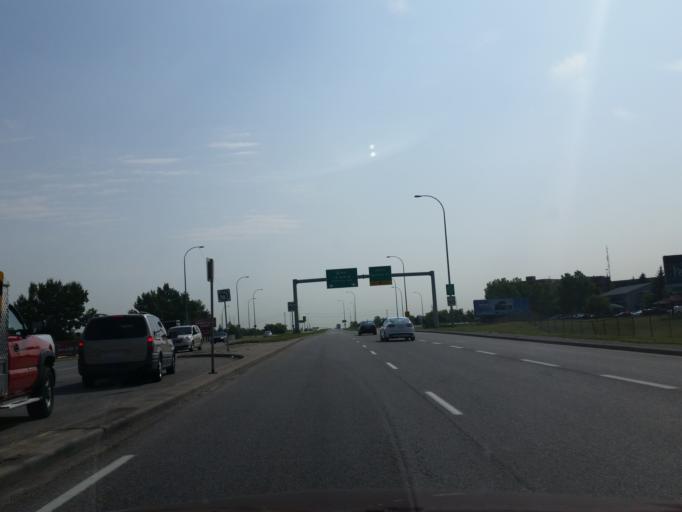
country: CA
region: Alberta
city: Calgary
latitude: 51.0669
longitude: -114.0107
